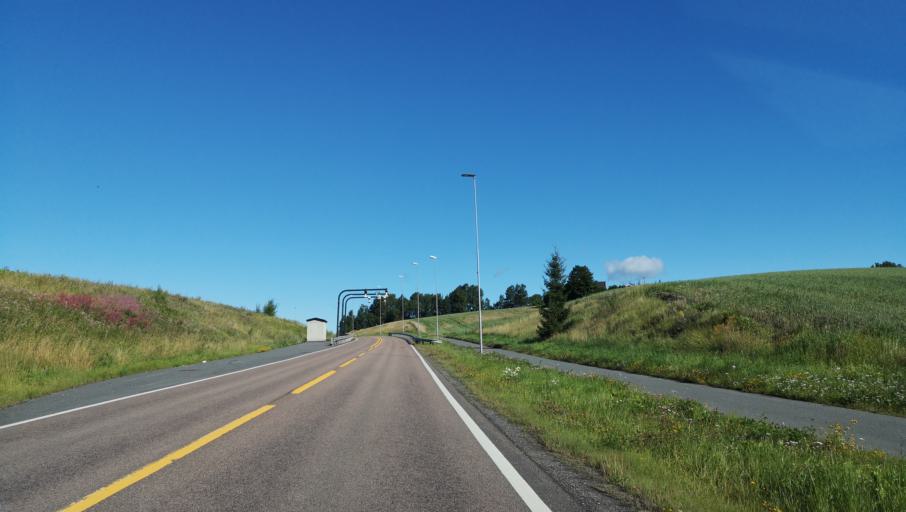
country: NO
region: Ostfold
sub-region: Spydeberg
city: Spydeberg
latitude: 59.6085
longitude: 11.0971
